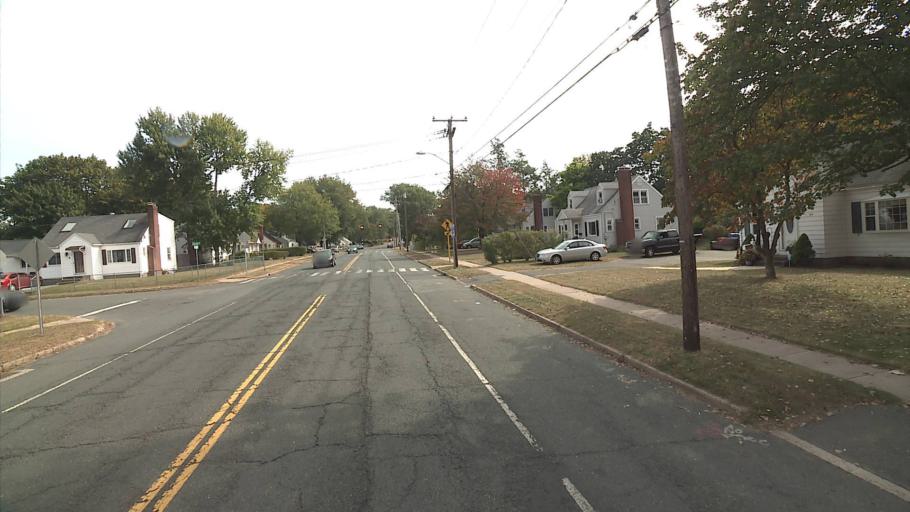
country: US
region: Connecticut
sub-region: Hartford County
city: Manchester
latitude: 41.7791
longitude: -72.5562
